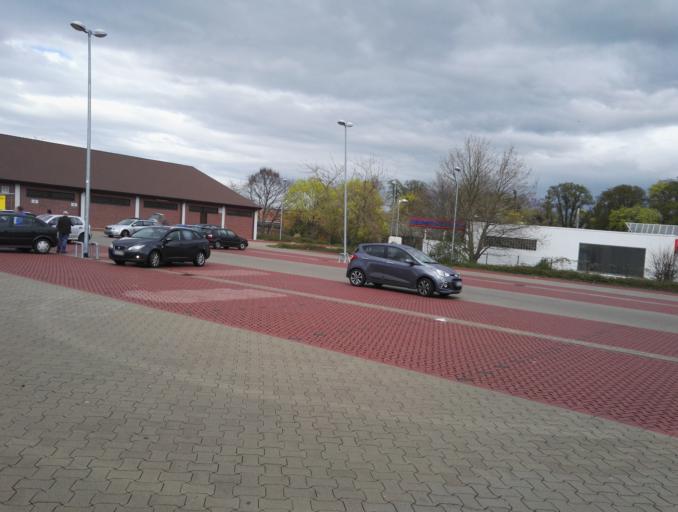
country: DE
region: Saxony-Anhalt
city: Halberstadt
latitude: 51.8976
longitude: 11.0623
